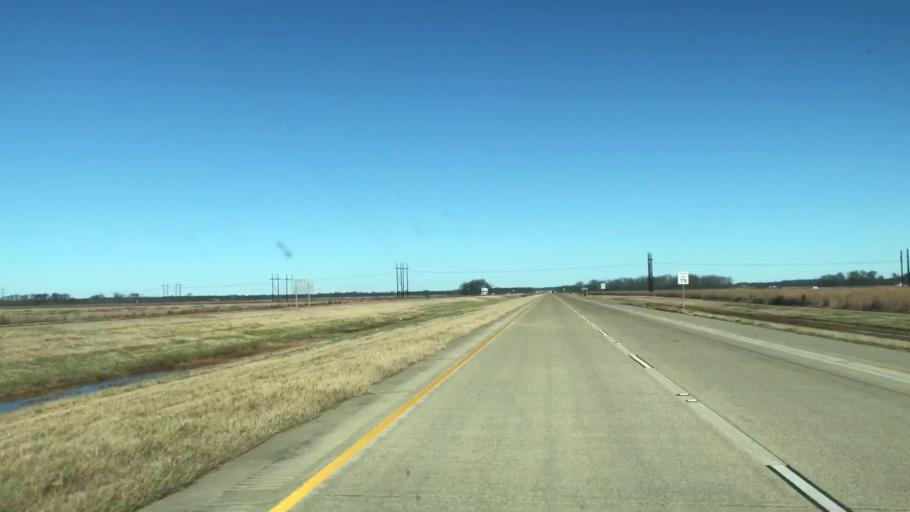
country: US
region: Louisiana
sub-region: Caddo Parish
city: Oil City
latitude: 32.7126
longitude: -93.8659
